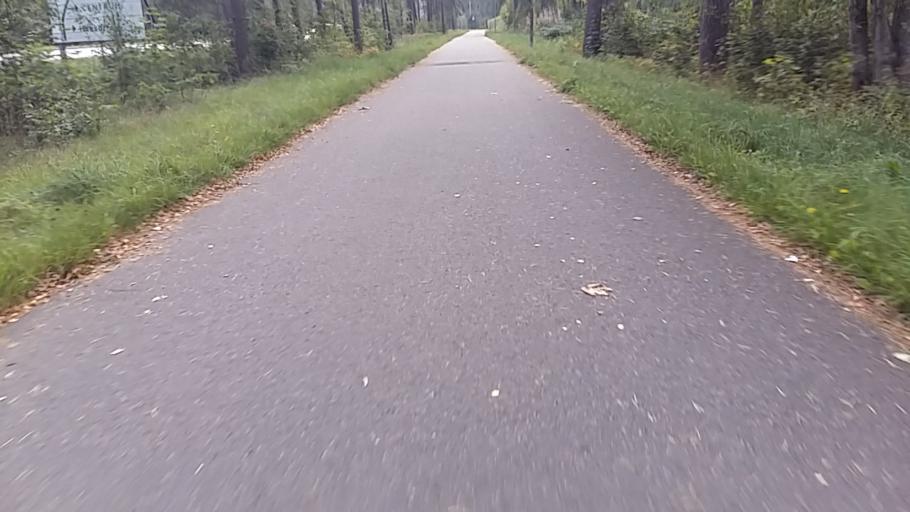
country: SE
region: Joenkoeping
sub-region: Jonkopings Kommun
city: Odensjo
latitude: 57.7443
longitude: 14.1568
